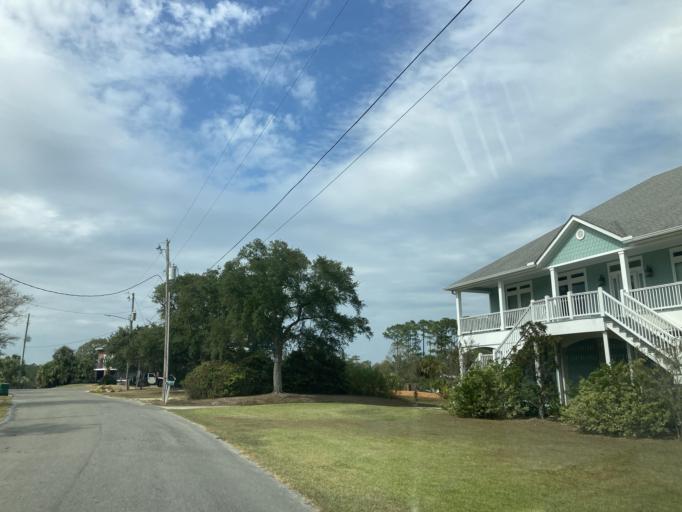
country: US
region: Mississippi
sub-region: Jackson County
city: Gulf Hills
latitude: 30.4351
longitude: -88.8461
